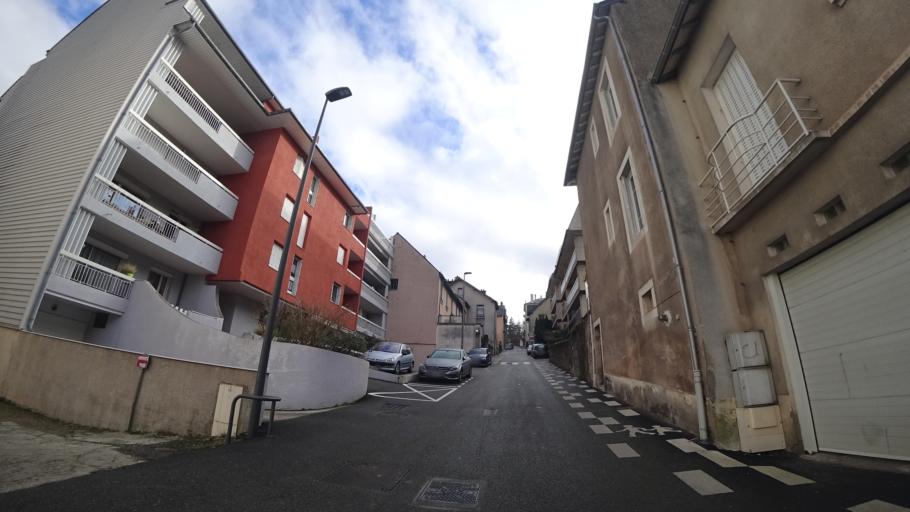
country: FR
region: Midi-Pyrenees
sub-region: Departement de l'Aveyron
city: Rodez
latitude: 44.3551
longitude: 2.5724
